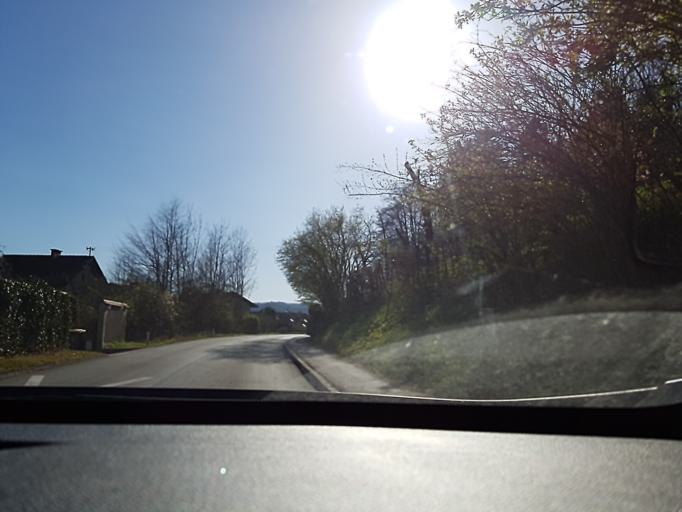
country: SI
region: Medvode
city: Zgornje Pirnice
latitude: 46.1221
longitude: 14.4748
